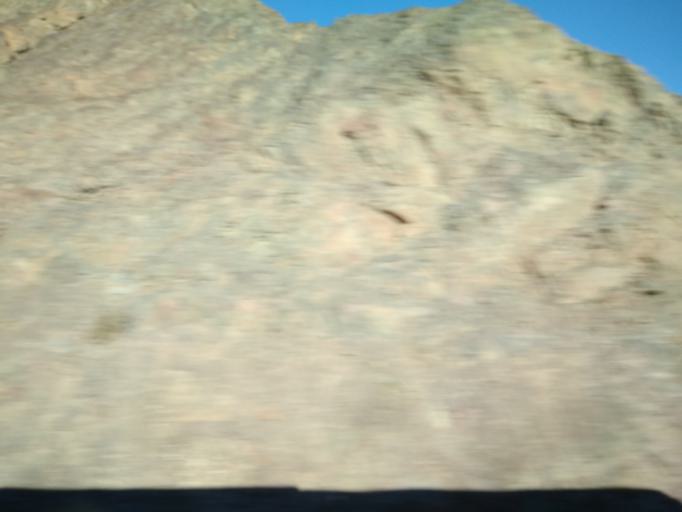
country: IL
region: Southern District
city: Eilat
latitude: 29.5674
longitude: 34.8932
